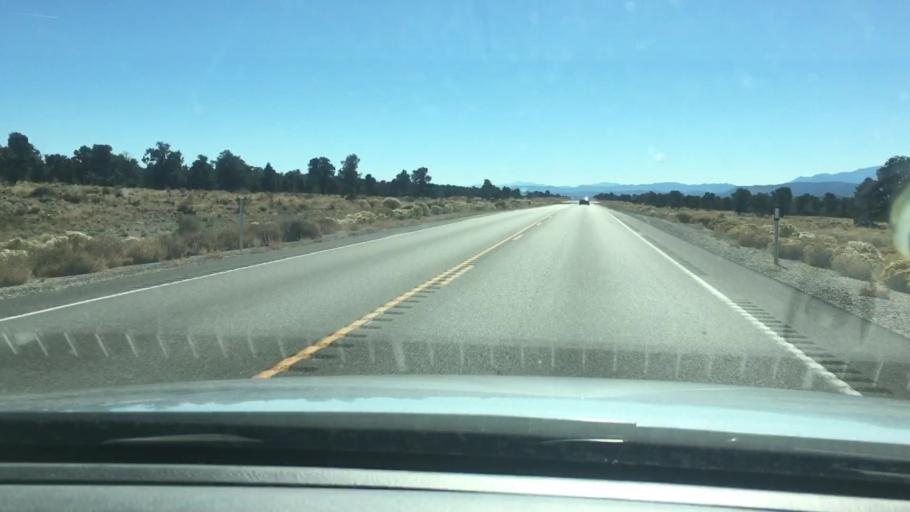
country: US
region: Nevada
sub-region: White Pine County
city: Ely
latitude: 39.1896
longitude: -115.0065
